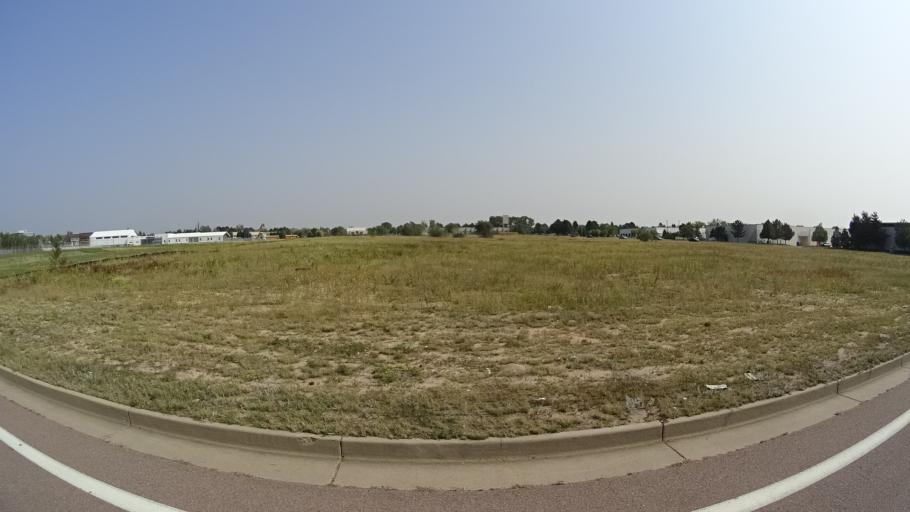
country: US
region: Colorado
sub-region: El Paso County
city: Stratmoor
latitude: 38.8075
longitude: -104.7545
